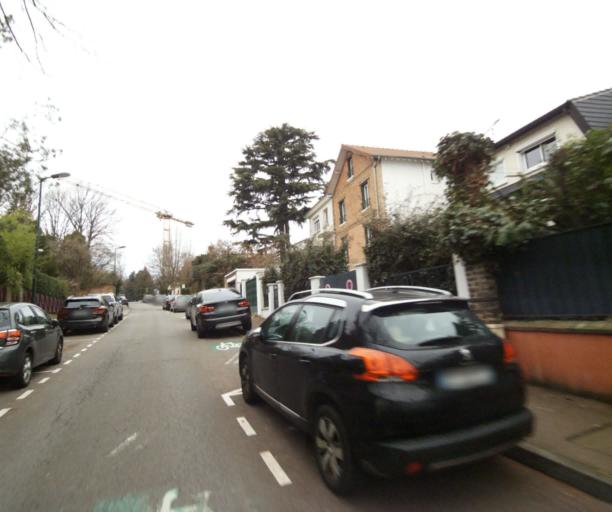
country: FR
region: Ile-de-France
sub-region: Departement des Hauts-de-Seine
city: Garches
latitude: 48.8468
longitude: 2.1831
